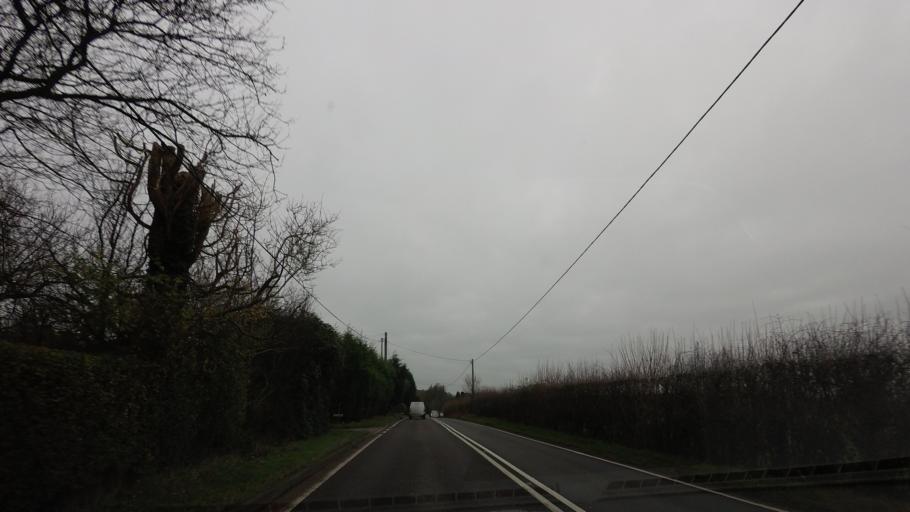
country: GB
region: England
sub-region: East Sussex
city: Saint Leonards-on-Sea
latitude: 50.9105
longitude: 0.5451
